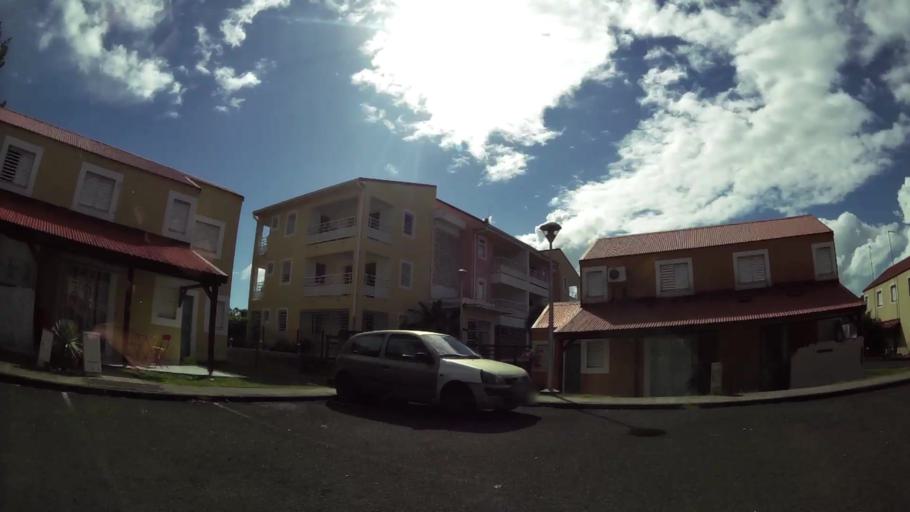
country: GP
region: Guadeloupe
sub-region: Guadeloupe
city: Port-Louis
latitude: 16.4167
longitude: -61.5247
